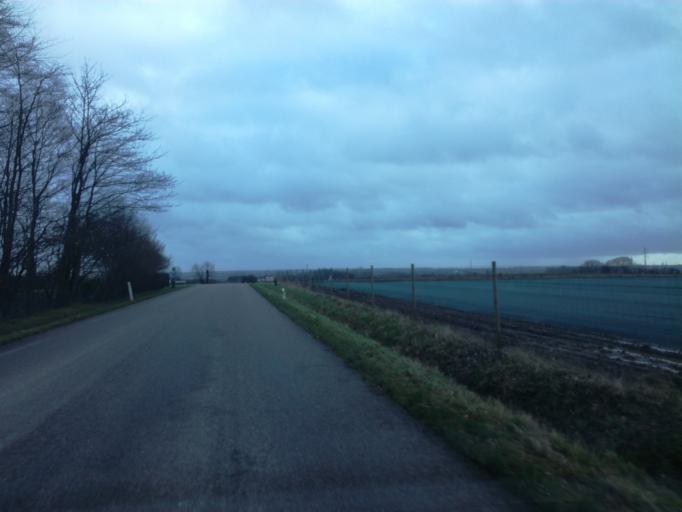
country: DK
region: South Denmark
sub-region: Vejle Kommune
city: Brejning
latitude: 55.6338
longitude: 9.6979
